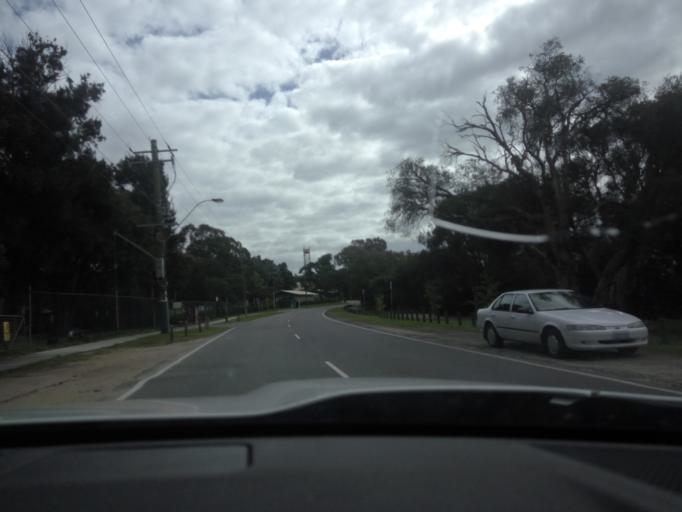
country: AU
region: Western Australia
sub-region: City of Cockburn
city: Bibra Lake
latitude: -32.0979
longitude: 115.8203
